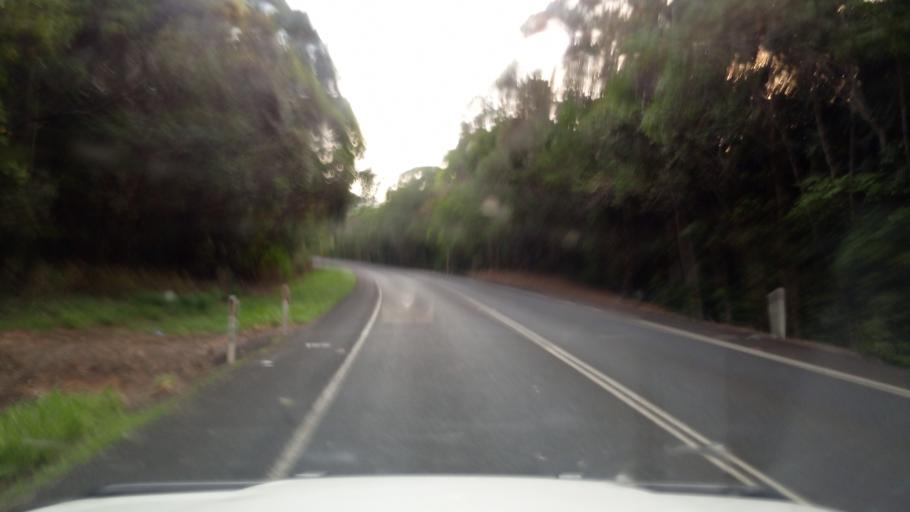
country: AU
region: Queensland
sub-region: Tablelands
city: Kuranda
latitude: -16.8477
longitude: 145.6029
